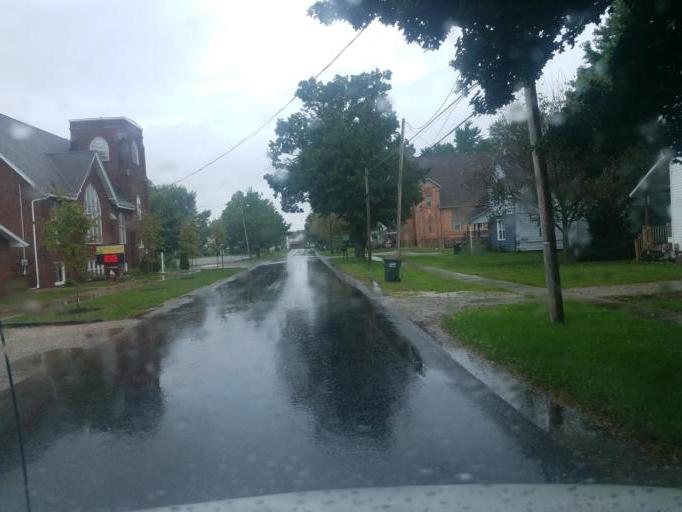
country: US
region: Ohio
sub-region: Wayne County
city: Creston
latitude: 40.9865
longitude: -81.8913
